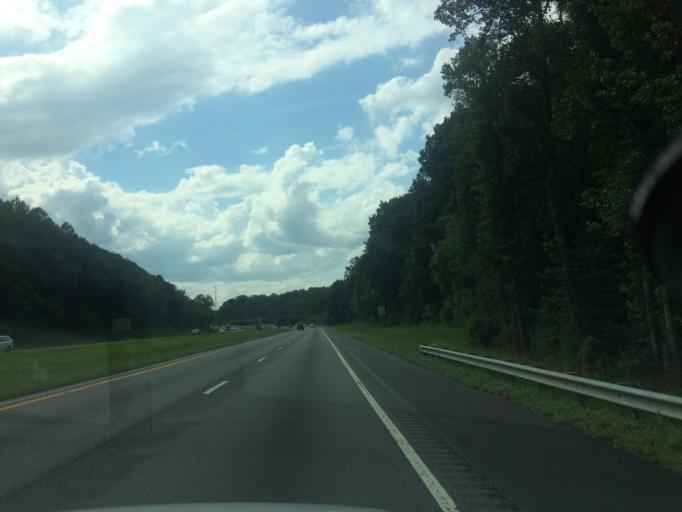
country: US
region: North Carolina
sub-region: Catawba County
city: Conover
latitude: 35.7066
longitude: -81.2738
